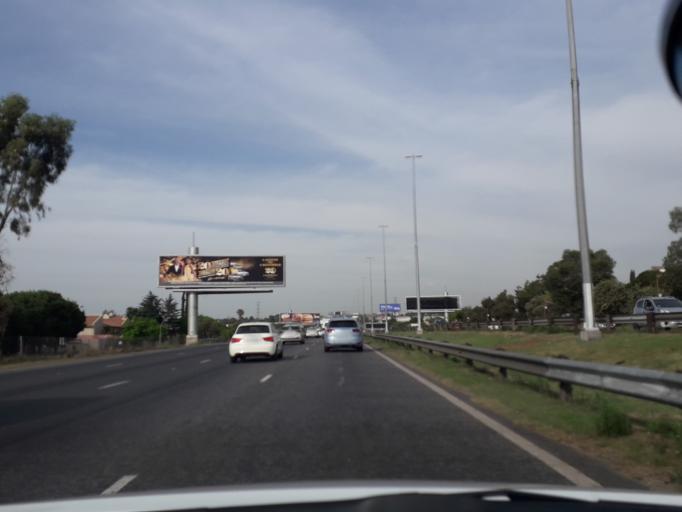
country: ZA
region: Gauteng
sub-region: City of Johannesburg Metropolitan Municipality
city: Modderfontein
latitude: -26.1503
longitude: 28.1721
